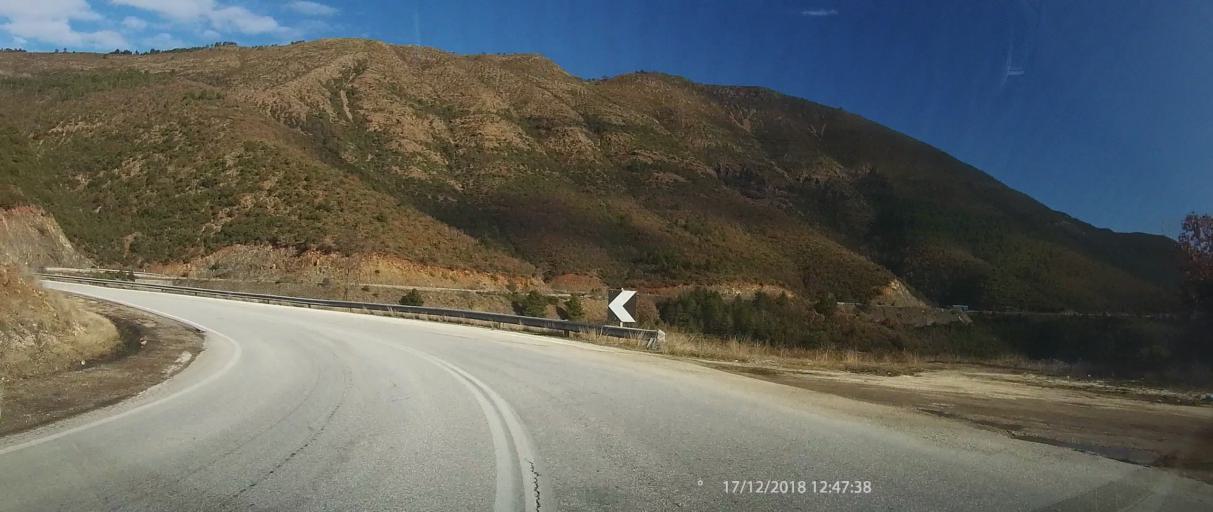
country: GR
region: Thessaly
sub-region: Trikala
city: Kastraki
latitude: 39.7838
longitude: 21.4305
